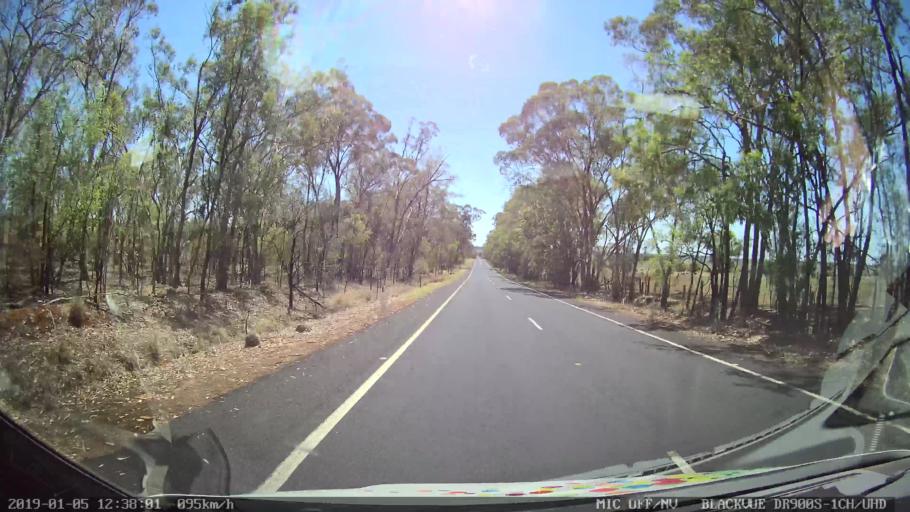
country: AU
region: New South Wales
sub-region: Warrumbungle Shire
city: Coonabarabran
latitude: -31.1992
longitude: 149.4626
